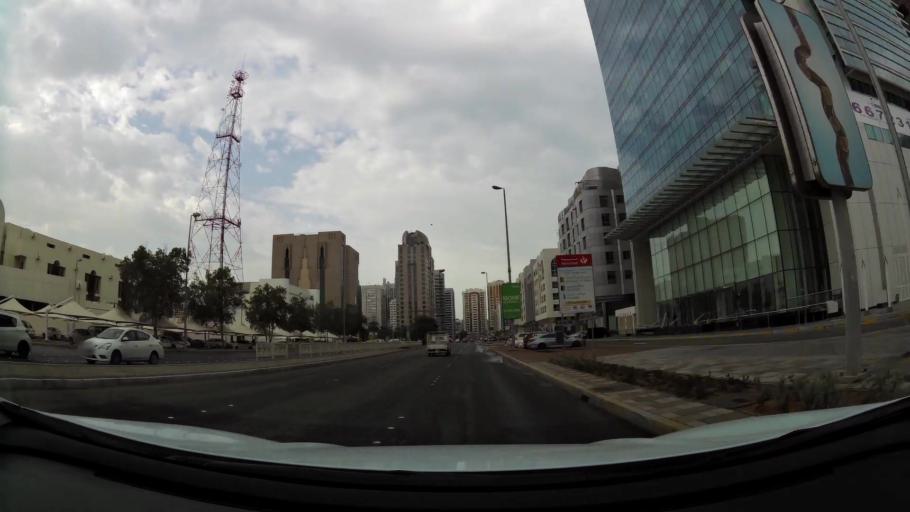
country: AE
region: Abu Dhabi
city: Abu Dhabi
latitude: 24.4915
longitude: 54.3767
